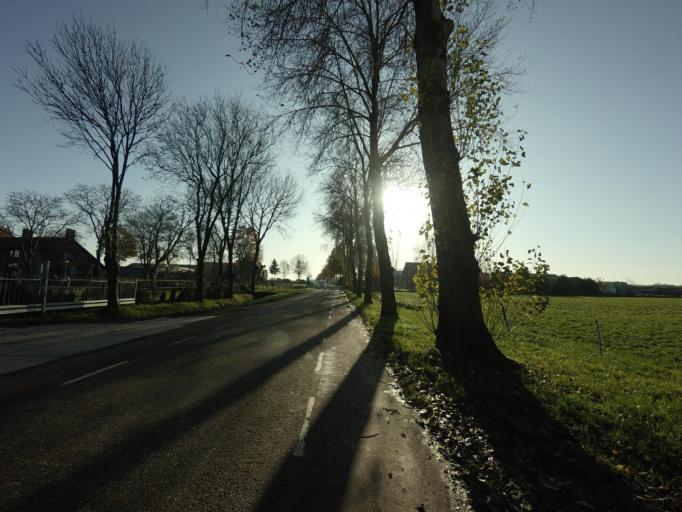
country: NL
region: Gelderland
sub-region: Gemeente Zaltbommel
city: Zaltbommel
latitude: 51.7849
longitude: 5.2741
